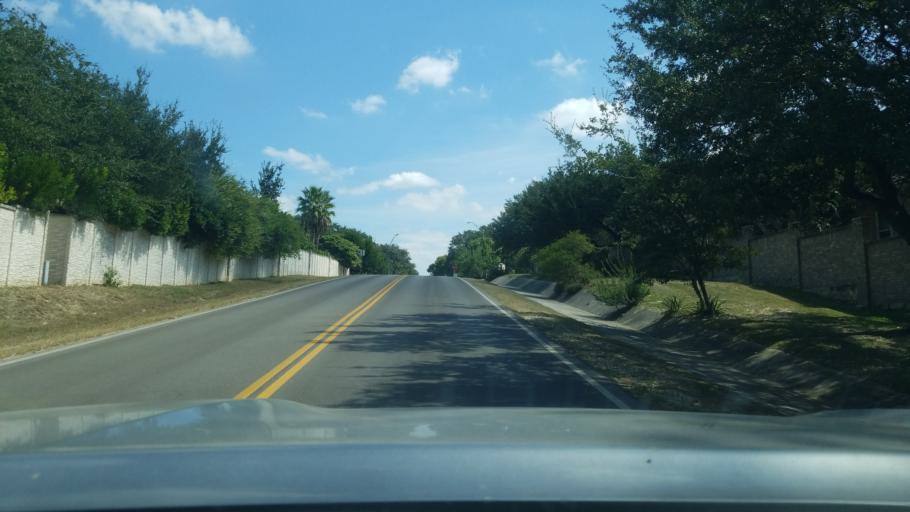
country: US
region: Texas
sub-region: Bexar County
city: Fair Oaks Ranch
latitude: 29.7311
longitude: -98.6439
